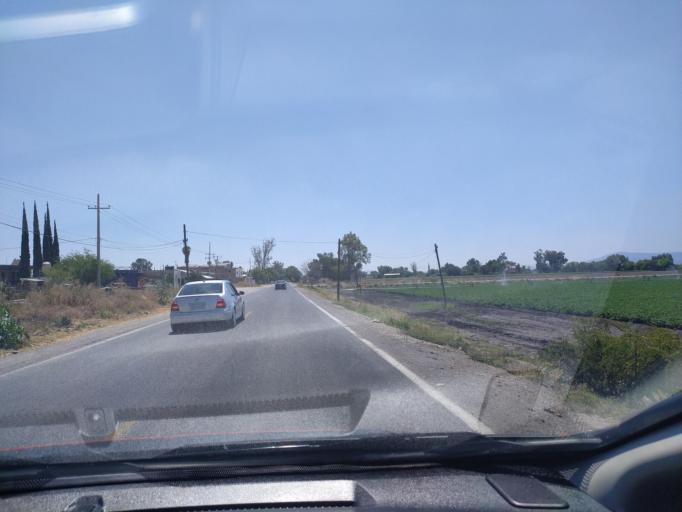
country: MX
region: Guanajuato
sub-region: San Francisco del Rincon
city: San Ignacio de Hidalgo
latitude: 20.8623
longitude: -101.8607
